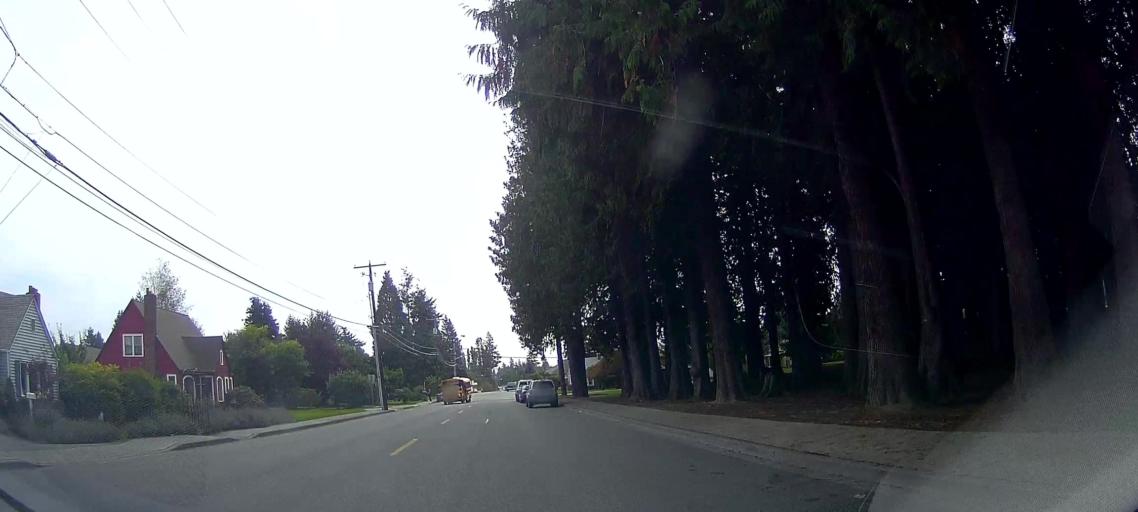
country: US
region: Washington
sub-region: Skagit County
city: Burlington
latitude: 48.4739
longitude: -122.3192
